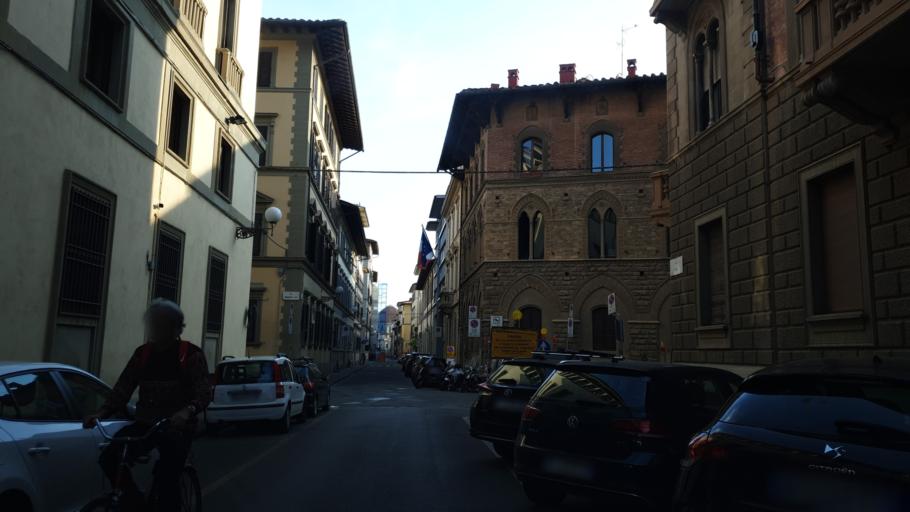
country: IT
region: Tuscany
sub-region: Province of Florence
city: Florence
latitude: 43.7817
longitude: 11.2588
